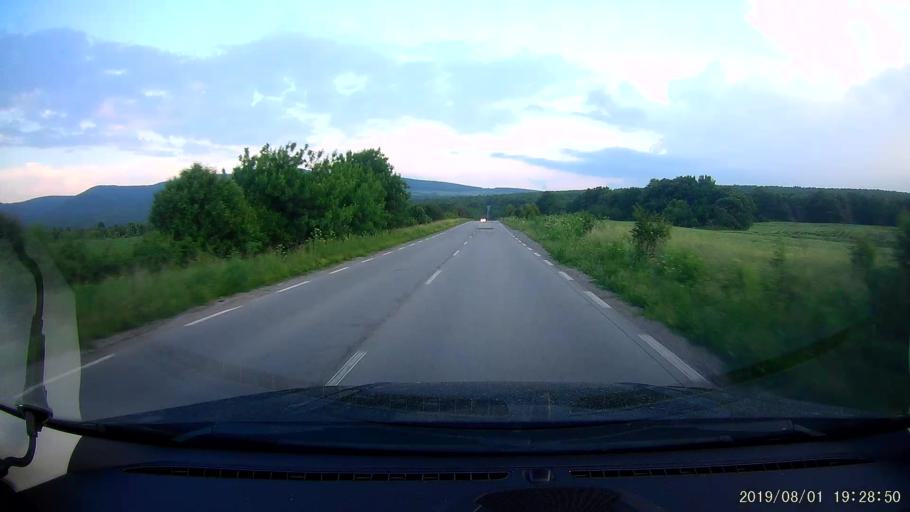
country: BG
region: Burgas
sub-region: Obshtina Sungurlare
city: Sungurlare
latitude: 42.8363
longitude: 26.9128
